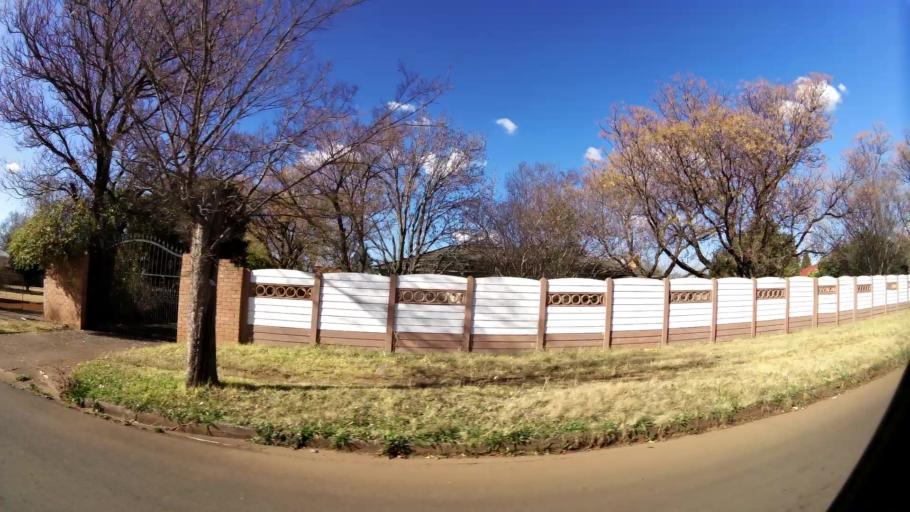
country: ZA
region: Gauteng
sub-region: West Rand District Municipality
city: Carletonville
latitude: -26.3684
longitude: 27.3949
